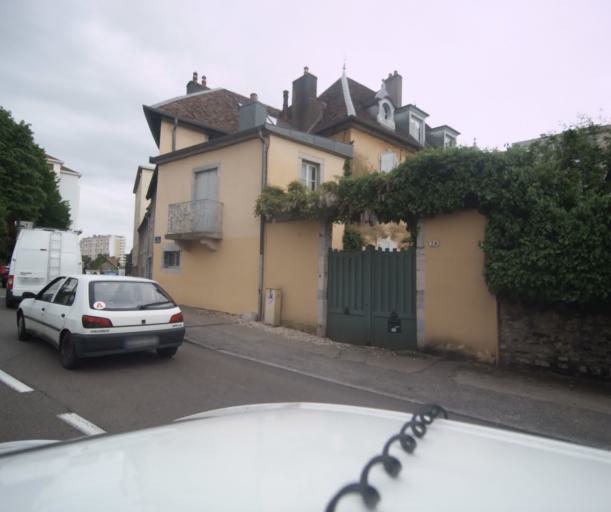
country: FR
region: Franche-Comte
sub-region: Departement du Doubs
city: Besancon
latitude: 47.2474
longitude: 6.0316
